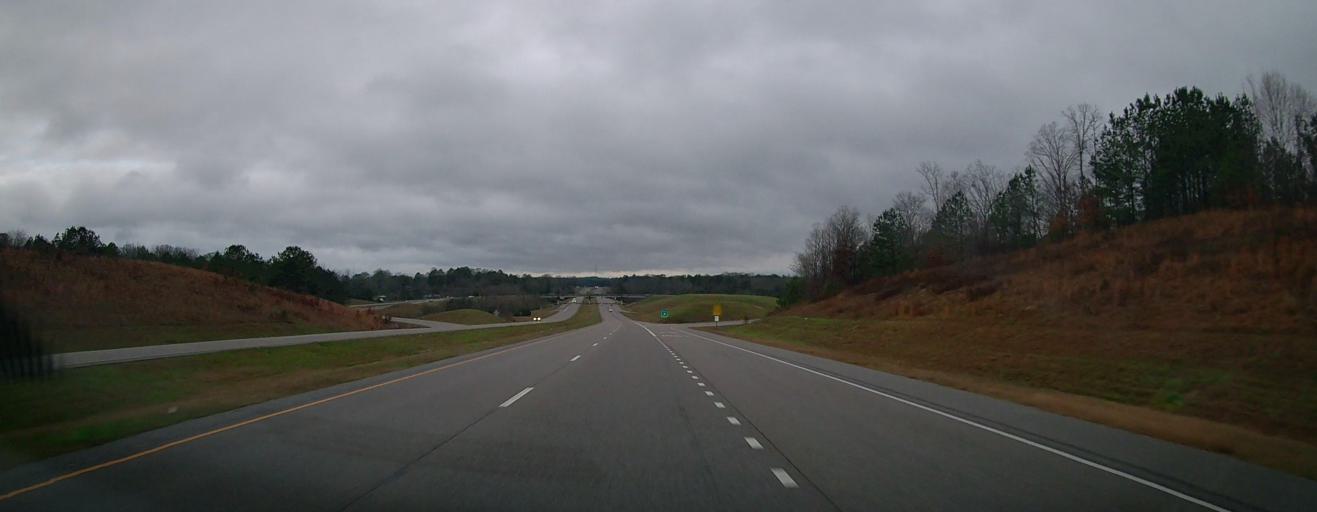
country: US
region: Alabama
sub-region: Bibb County
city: Centreville
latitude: 32.9571
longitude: -87.1285
